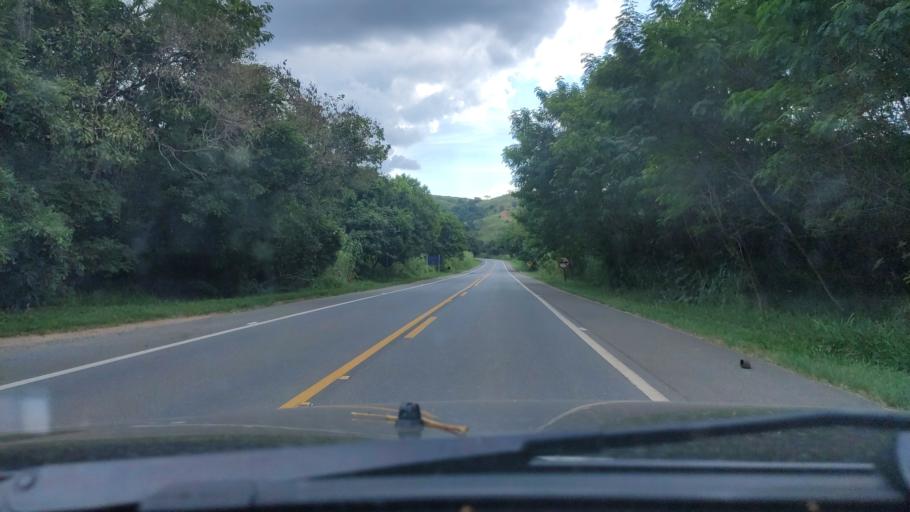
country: BR
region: Sao Paulo
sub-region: Aguas De Lindoia
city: Aguas de Lindoia
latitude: -22.4711
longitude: -46.6992
